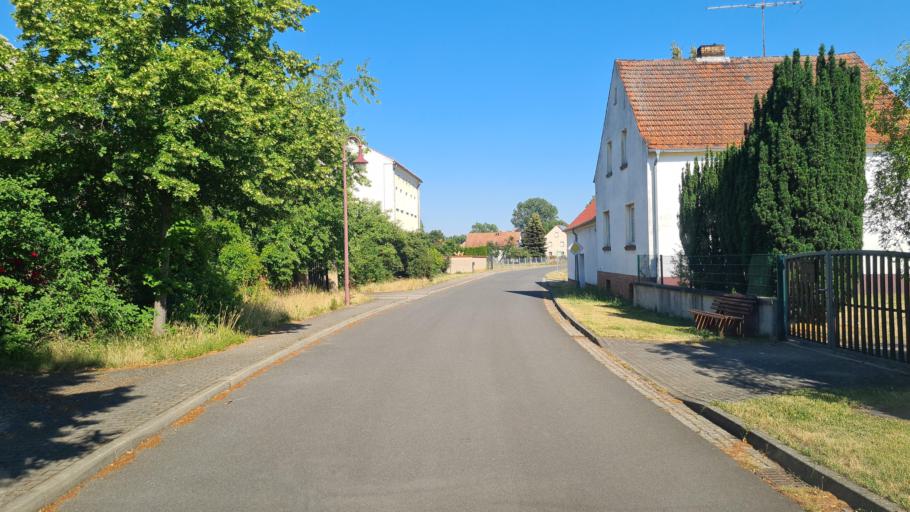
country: DE
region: Saxony-Anhalt
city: Prettin
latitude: 51.6979
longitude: 12.9523
